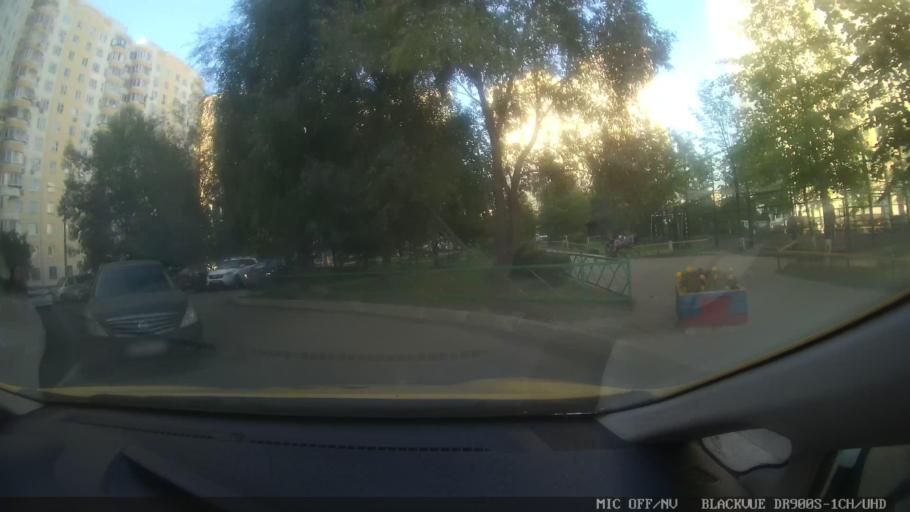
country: RU
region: Moscow
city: Nekrasovka
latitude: 55.6963
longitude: 37.9077
